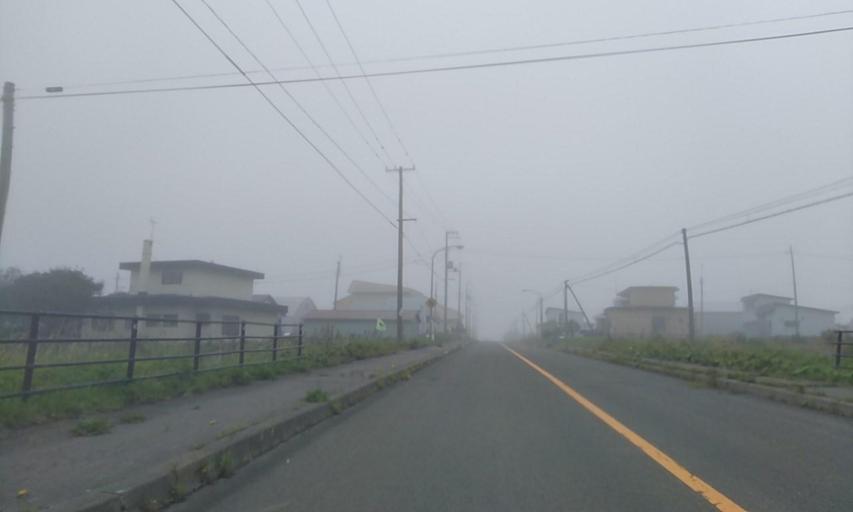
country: JP
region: Hokkaido
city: Nemuro
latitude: 43.3655
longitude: 145.7966
